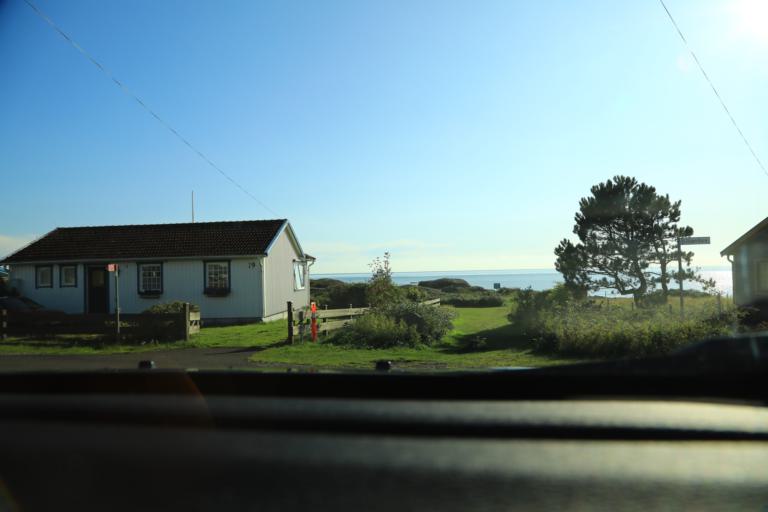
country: SE
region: Halland
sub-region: Varbergs Kommun
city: Varberg
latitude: 57.1165
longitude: 12.2088
